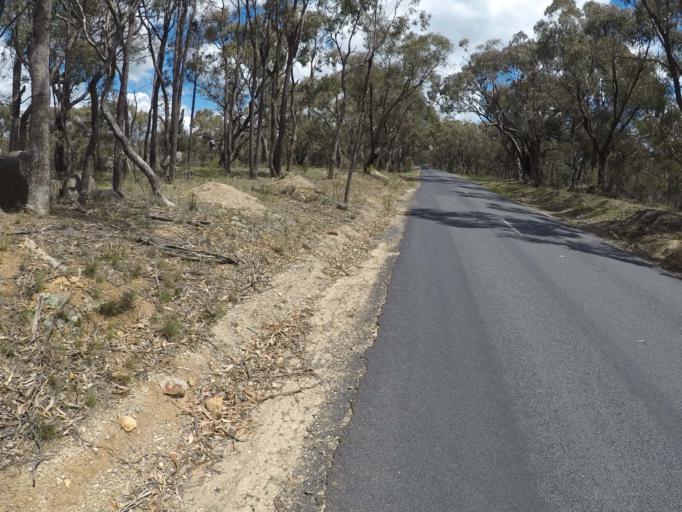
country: AU
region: New South Wales
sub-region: Blayney
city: Blayney
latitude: -33.5810
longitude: 149.3940
